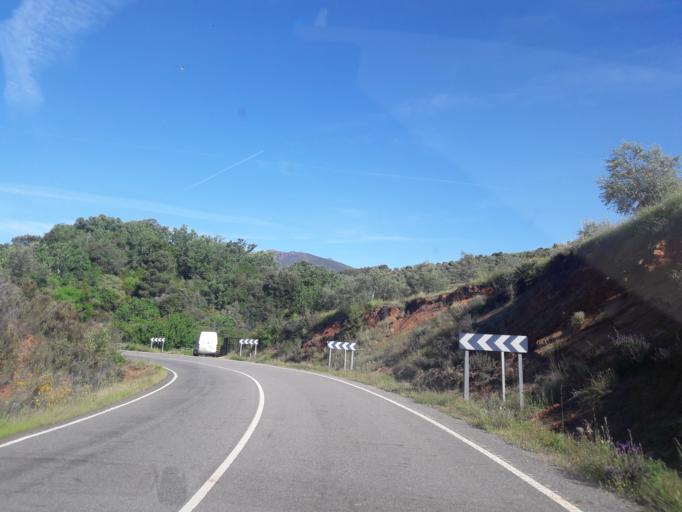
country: ES
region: Castille and Leon
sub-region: Provincia de Salamanca
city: Sotoserrano
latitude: 40.4255
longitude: -6.0365
